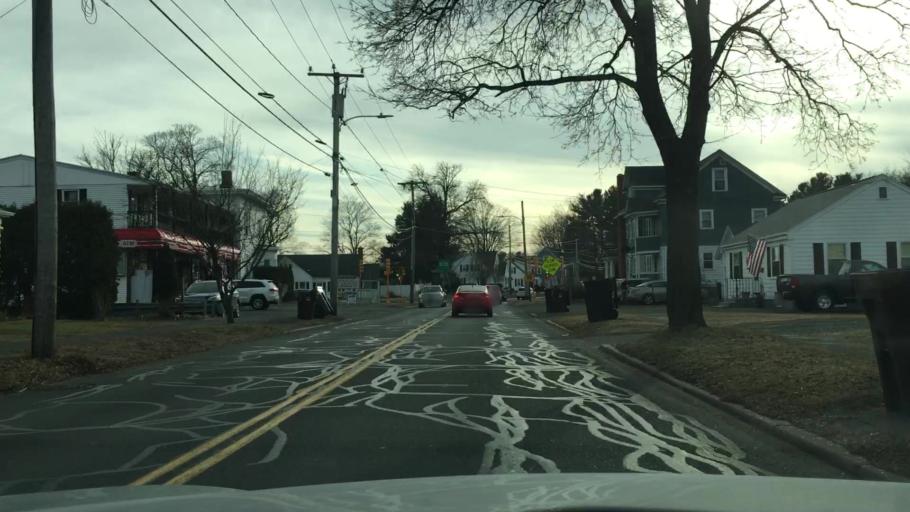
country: US
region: Massachusetts
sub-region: Hampden County
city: Westfield
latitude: 42.1156
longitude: -72.7526
